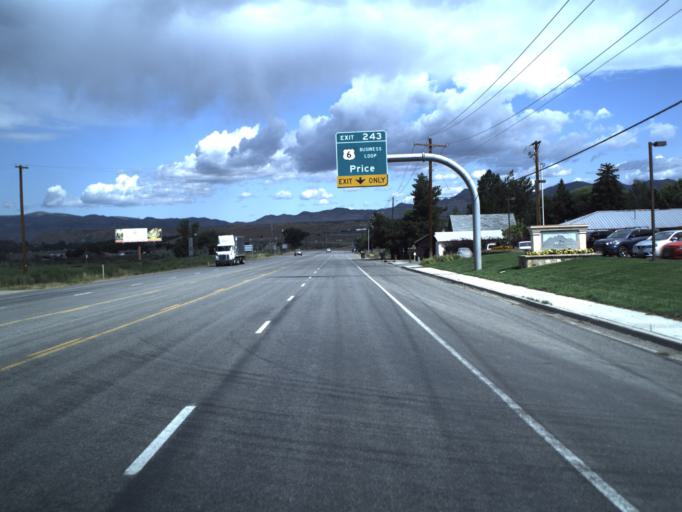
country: US
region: Utah
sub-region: Carbon County
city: Price
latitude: 39.5779
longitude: -110.7855
